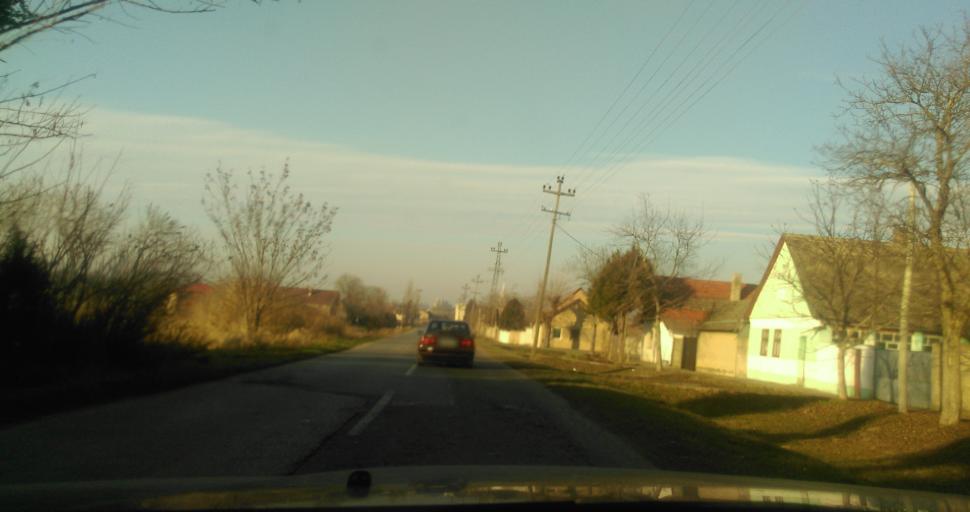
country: RS
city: Backo Gradiste
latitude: 45.5264
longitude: 20.0248
